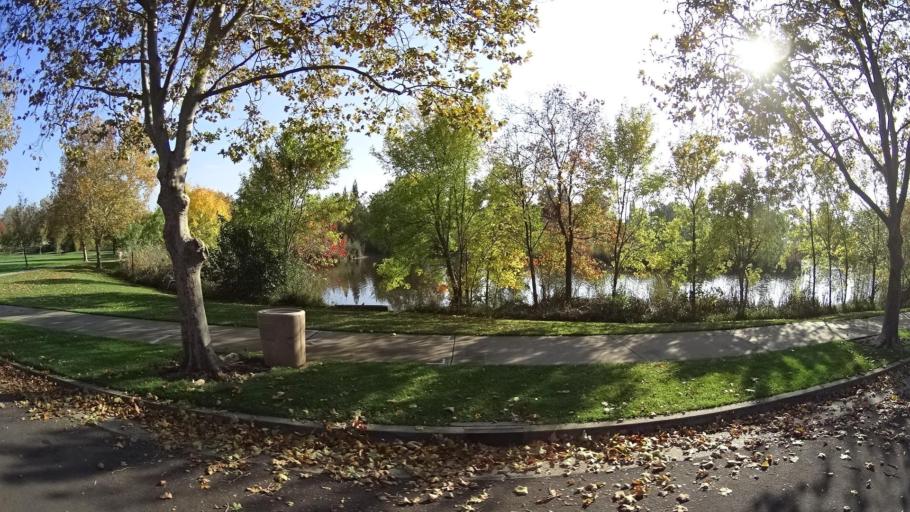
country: US
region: California
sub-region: Sacramento County
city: Elk Grove
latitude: 38.4245
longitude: -121.3761
